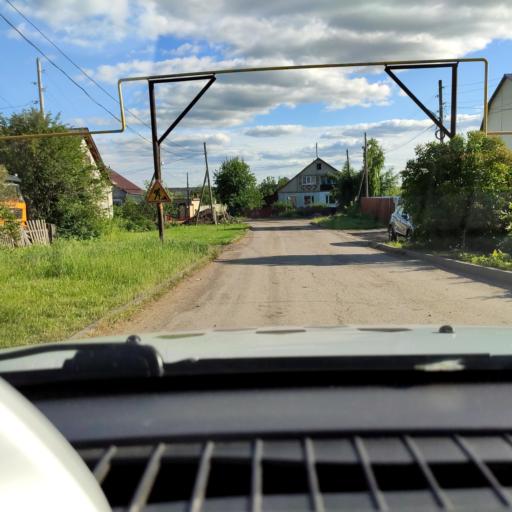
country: RU
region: Perm
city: Froly
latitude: 57.9176
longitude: 56.2758
